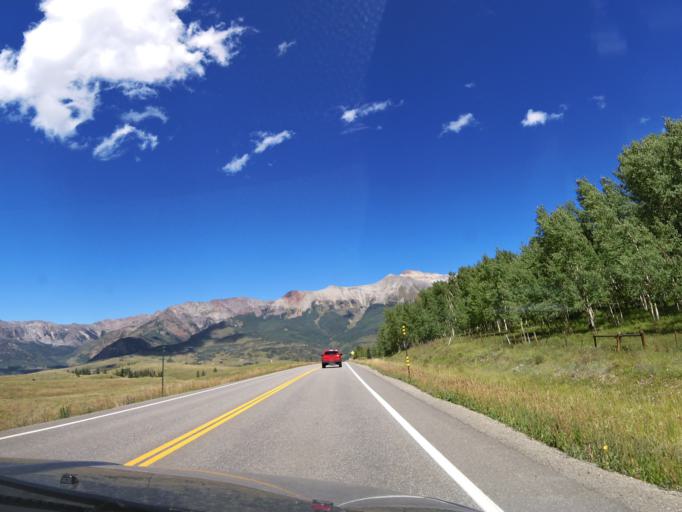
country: US
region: Colorado
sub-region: San Miguel County
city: Mountain Village
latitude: 37.9224
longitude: -107.8837
